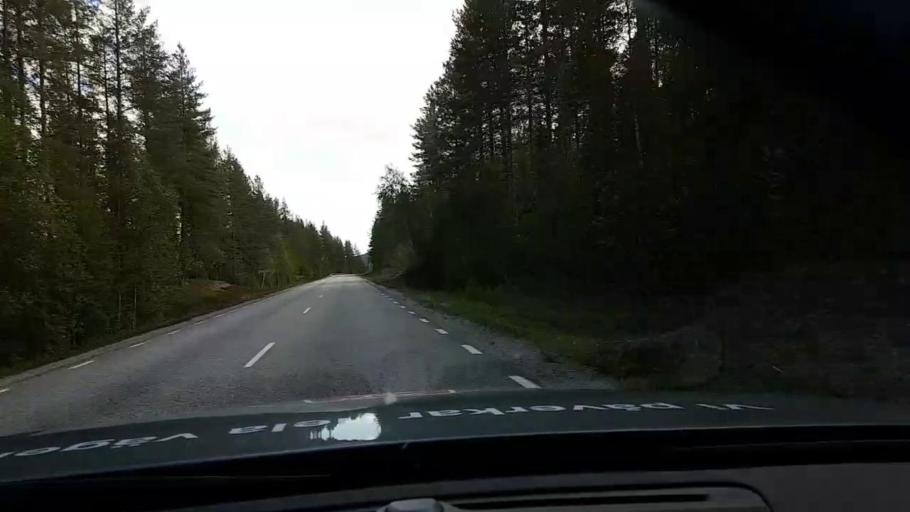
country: SE
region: Vaesternorrland
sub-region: OErnskoeldsviks Kommun
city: Bredbyn
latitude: 63.6930
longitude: 17.7674
